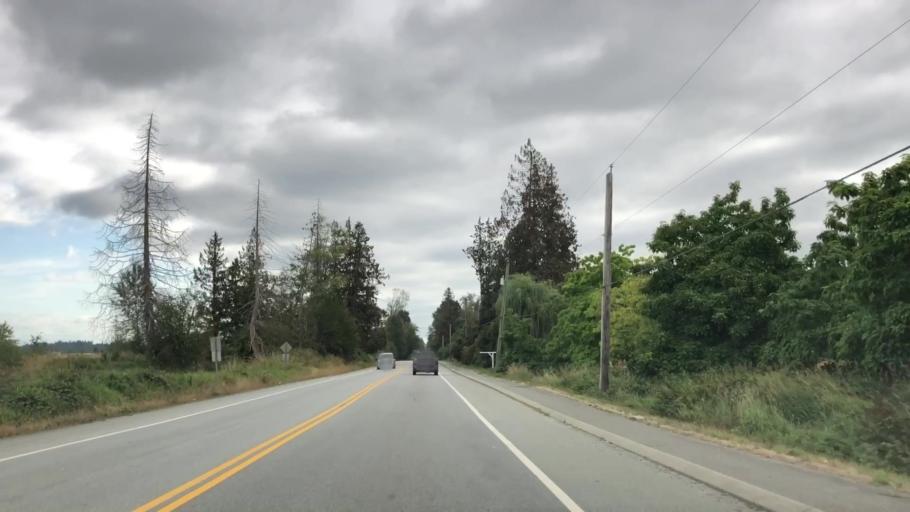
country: US
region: Washington
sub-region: Whatcom County
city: Blaine
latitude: 49.0601
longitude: -122.7448
